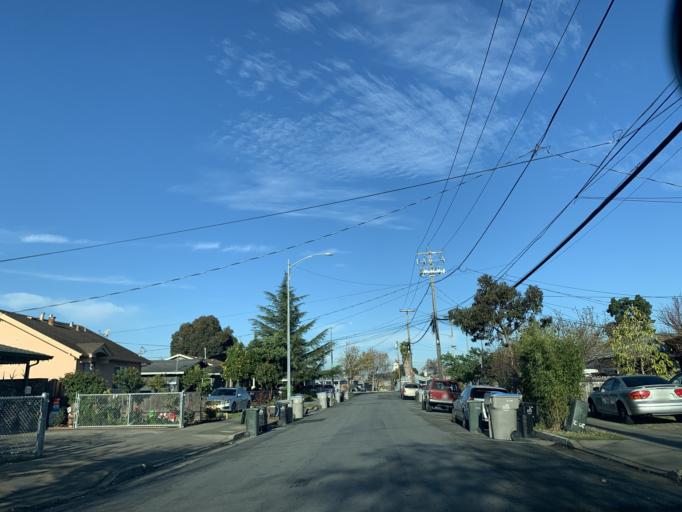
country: US
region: California
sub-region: Santa Clara County
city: San Jose
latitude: 37.3450
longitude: -121.8598
